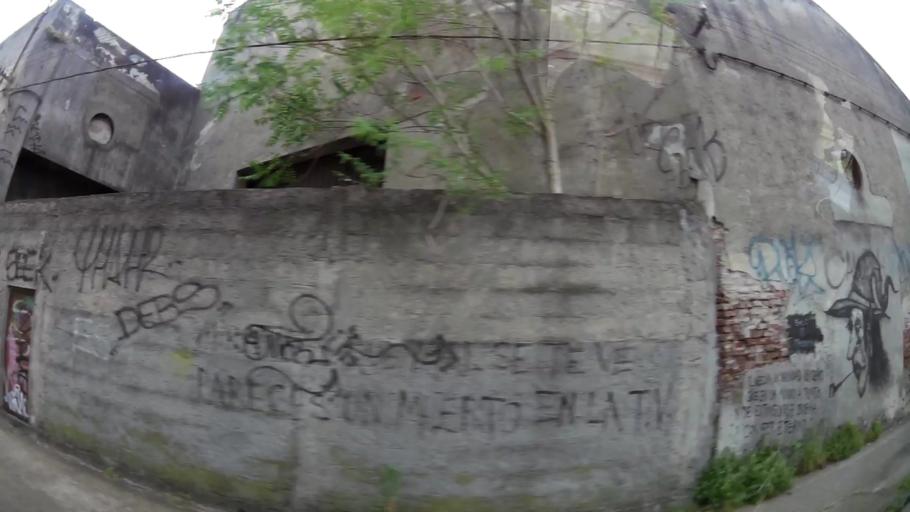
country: UY
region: Montevideo
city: Montevideo
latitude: -34.8839
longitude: -56.1967
